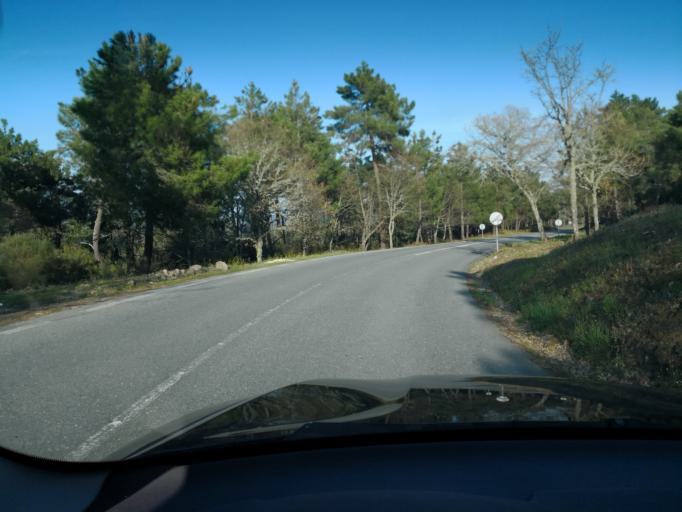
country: PT
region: Vila Real
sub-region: Sabrosa
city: Sabrosa
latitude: 41.3578
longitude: -7.6302
